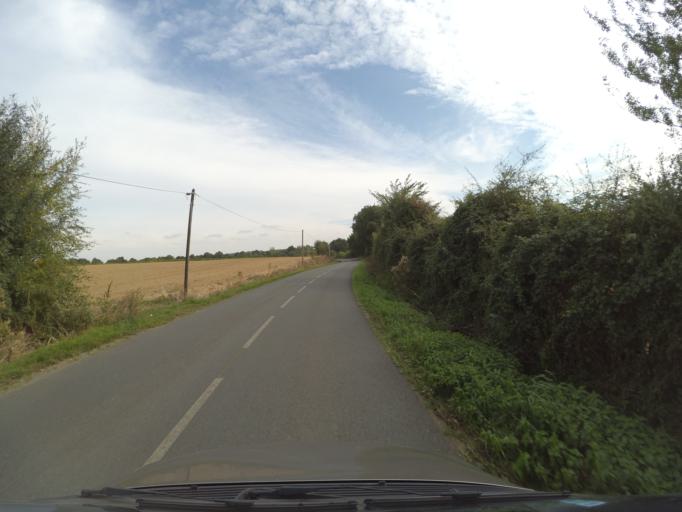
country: FR
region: Pays de la Loire
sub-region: Departement de Maine-et-Loire
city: Vihiers
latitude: 47.2071
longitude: -0.5528
